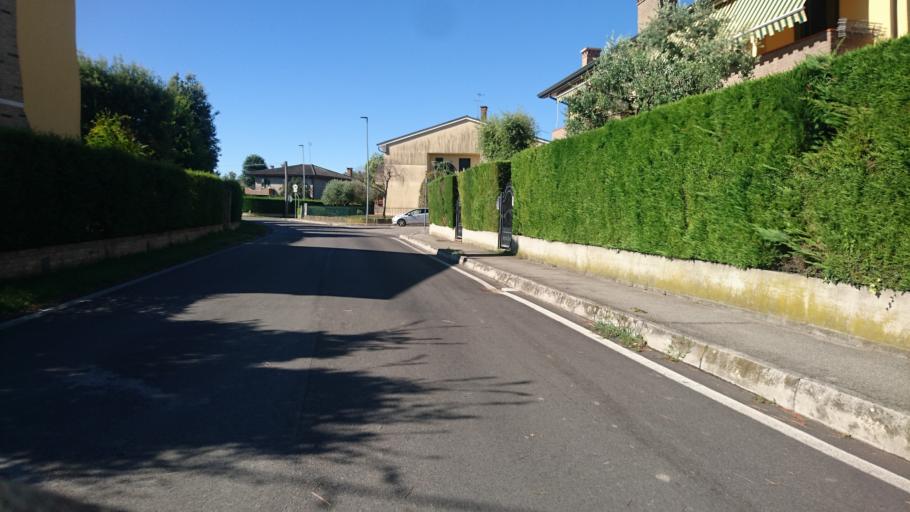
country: IT
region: Veneto
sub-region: Provincia di Padova
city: Legnaro
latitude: 45.3381
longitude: 11.9670
